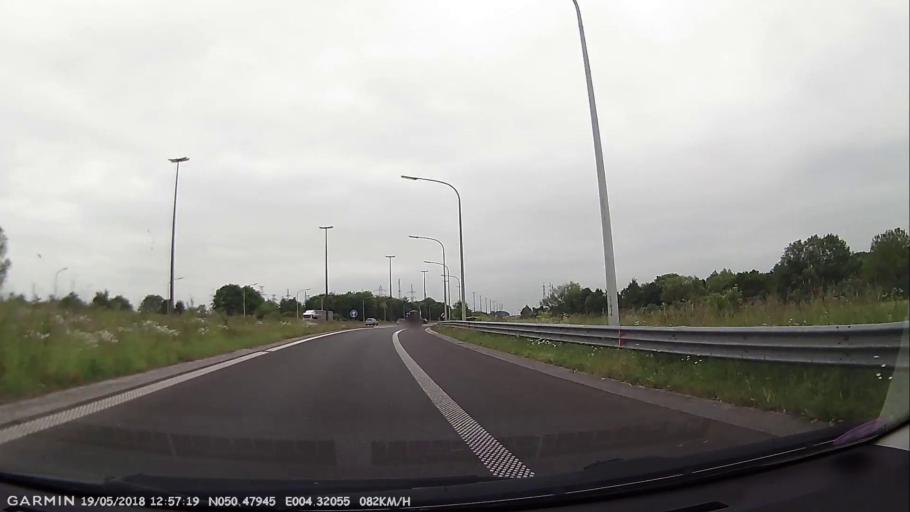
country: BE
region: Wallonia
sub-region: Province du Hainaut
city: Chapelle-lez-Herlaimont
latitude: 50.4795
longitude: 4.3206
